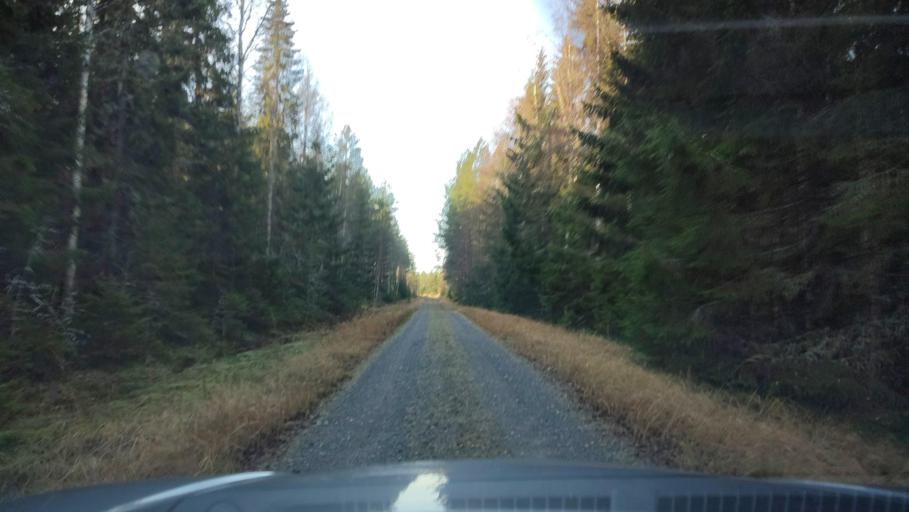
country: FI
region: Southern Ostrobothnia
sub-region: Suupohja
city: Karijoki
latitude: 62.1970
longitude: 21.6104
